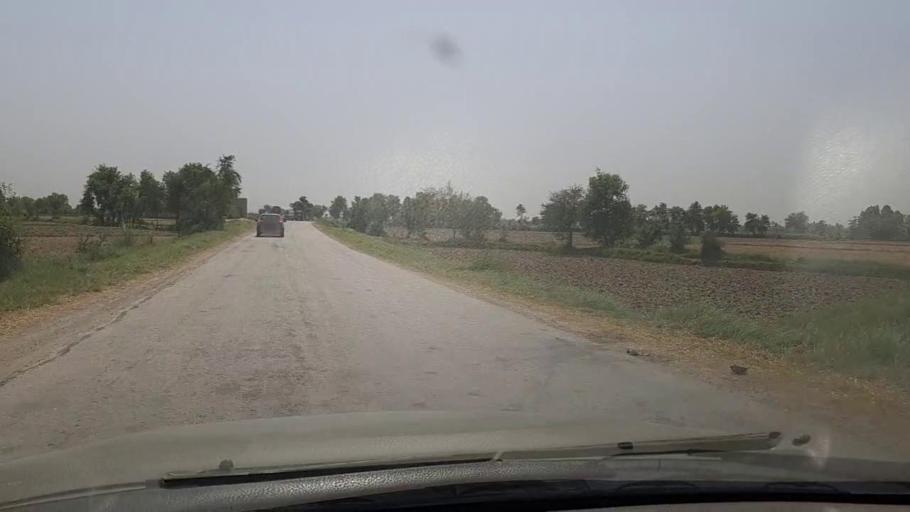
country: PK
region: Sindh
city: Kambar
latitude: 27.6223
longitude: 68.0230
